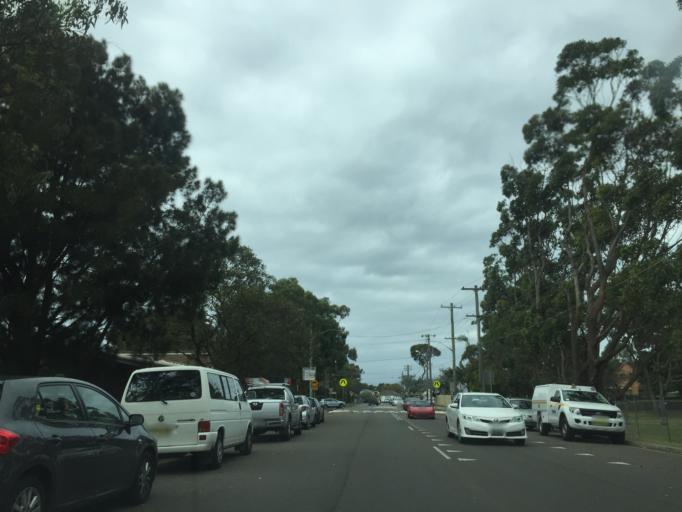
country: AU
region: New South Wales
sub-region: Pittwater
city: Warriewood
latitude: -33.6973
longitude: 151.2980
